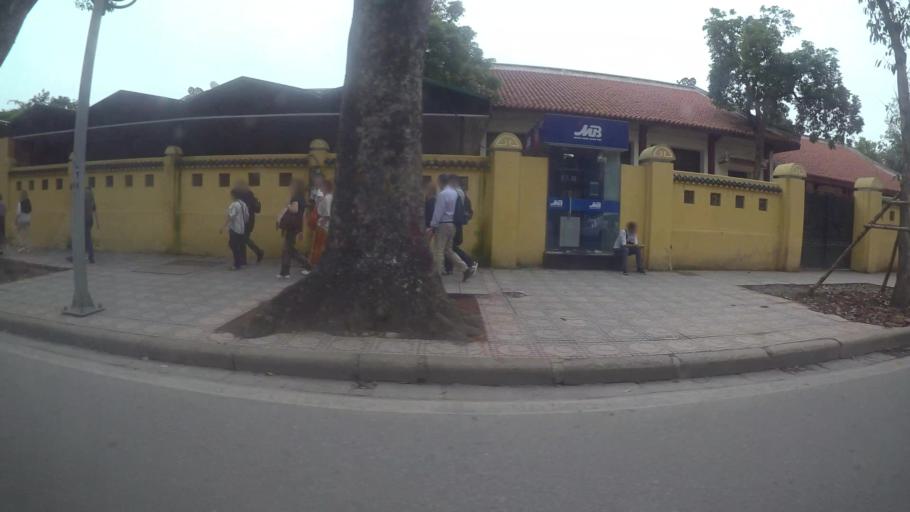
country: VN
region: Ha Noi
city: Hanoi
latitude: 21.0342
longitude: 105.8341
